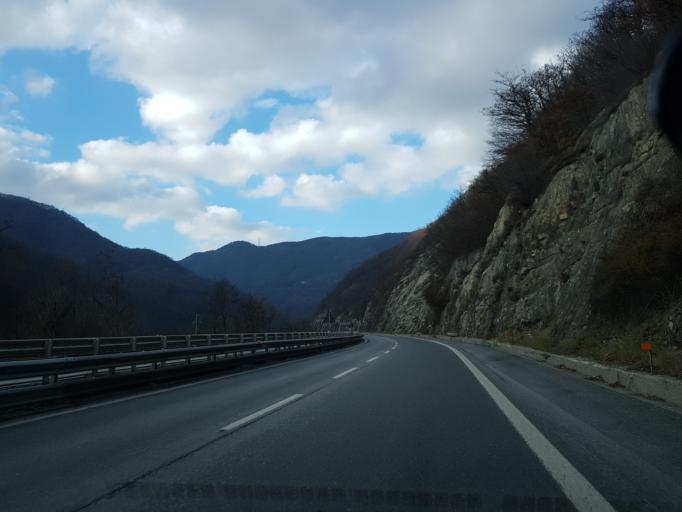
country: IT
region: Liguria
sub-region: Provincia di Genova
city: Ronco Scrivia
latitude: 44.6246
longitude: 8.9505
